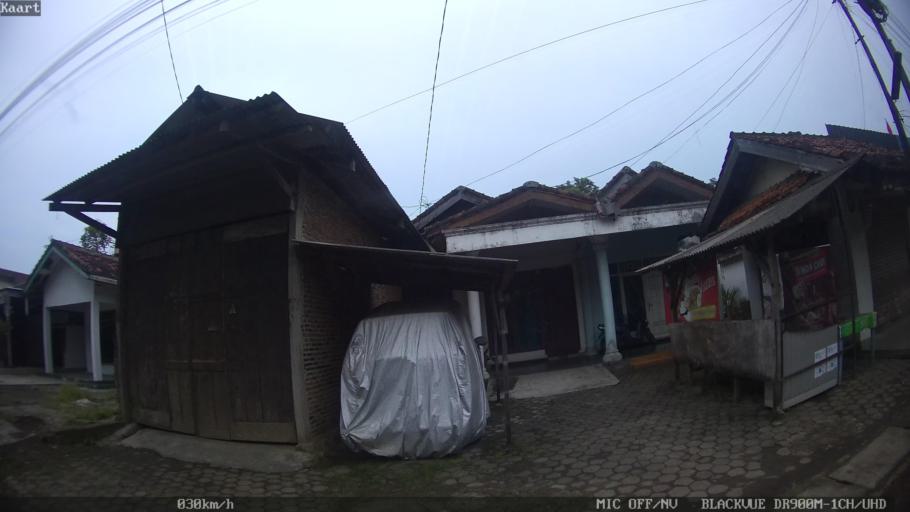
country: ID
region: Lampung
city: Kedaton
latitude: -5.3863
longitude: 105.2455
